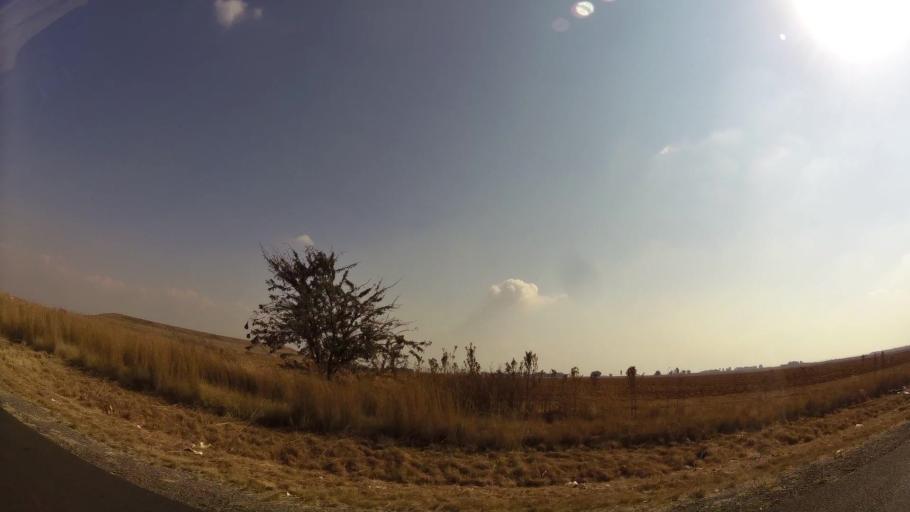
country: ZA
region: Mpumalanga
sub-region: Nkangala District Municipality
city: Delmas
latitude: -26.1479
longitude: 28.5315
